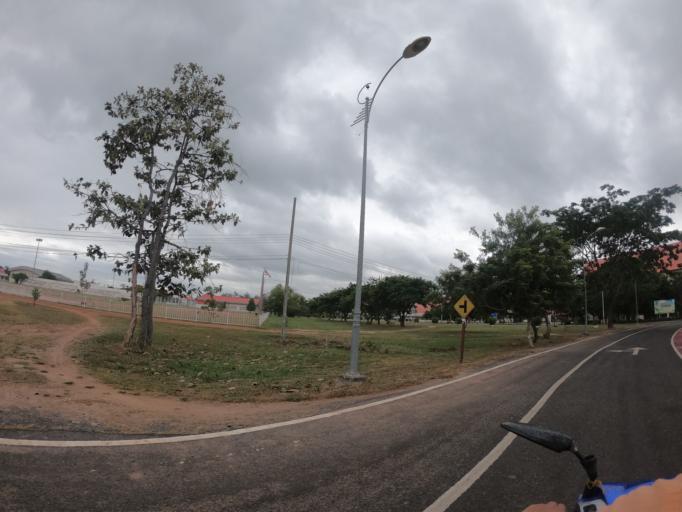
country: TH
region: Roi Et
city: Selaphum
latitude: 16.1429
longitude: 103.8811
